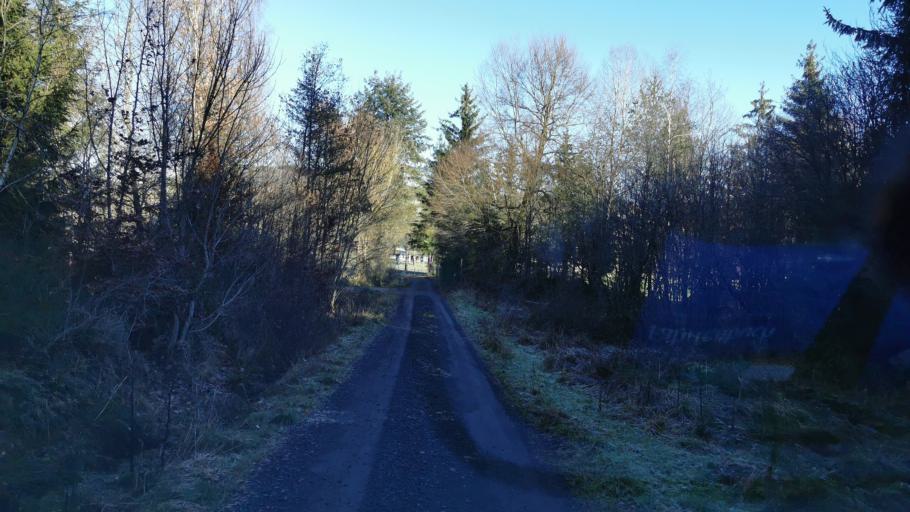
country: DE
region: Rheinland-Pfalz
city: Weidenbach
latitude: 50.1256
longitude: 6.7031
